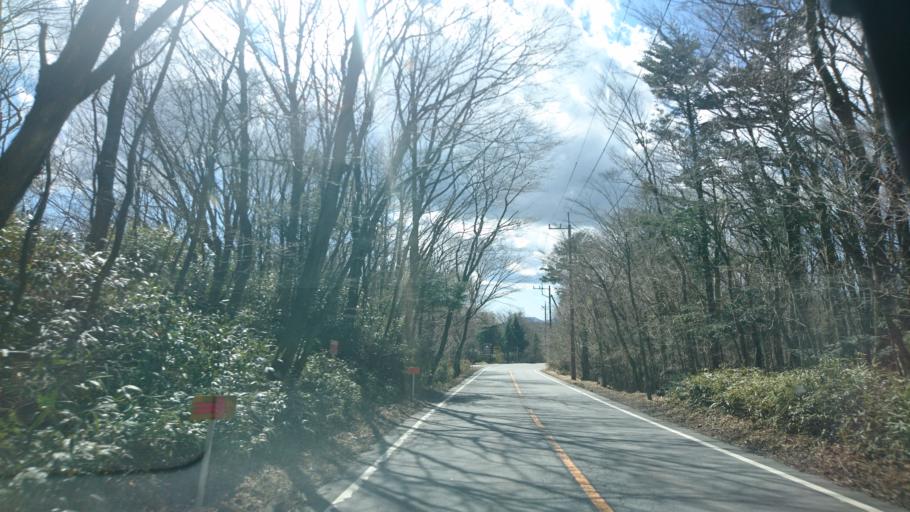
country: JP
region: Yamanashi
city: Fujikawaguchiko
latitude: 35.4303
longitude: 138.6339
